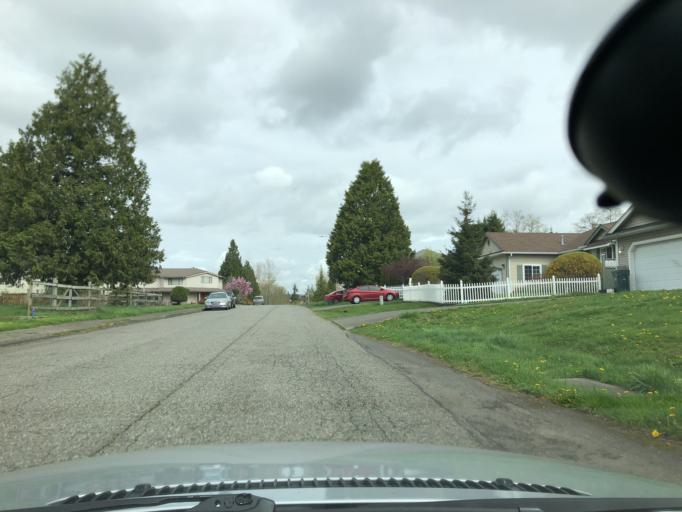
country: US
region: Washington
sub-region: Whatcom County
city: Blaine
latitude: 48.9991
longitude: -122.7400
